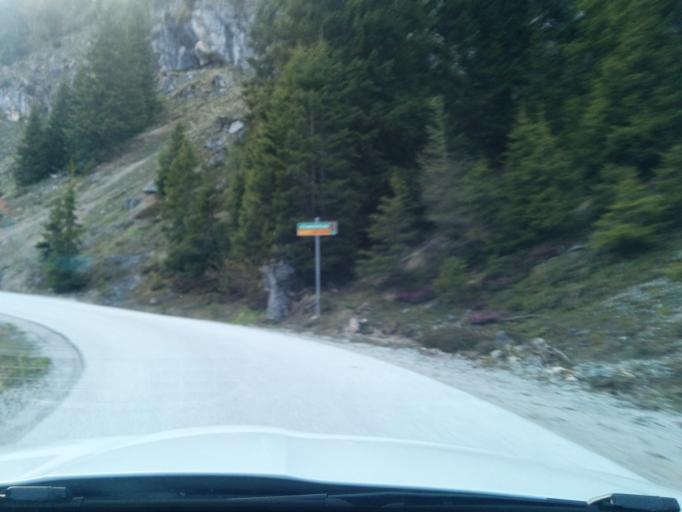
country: AT
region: Styria
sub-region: Politischer Bezirk Liezen
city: Aich
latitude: 47.4539
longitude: 13.8231
